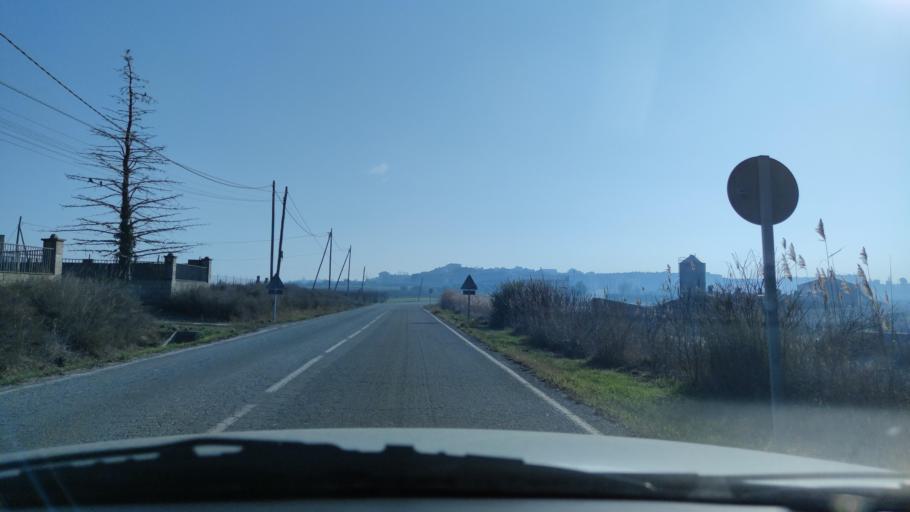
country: ES
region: Catalonia
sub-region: Provincia de Lleida
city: Alcoletge
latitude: 41.6199
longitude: 0.7319
